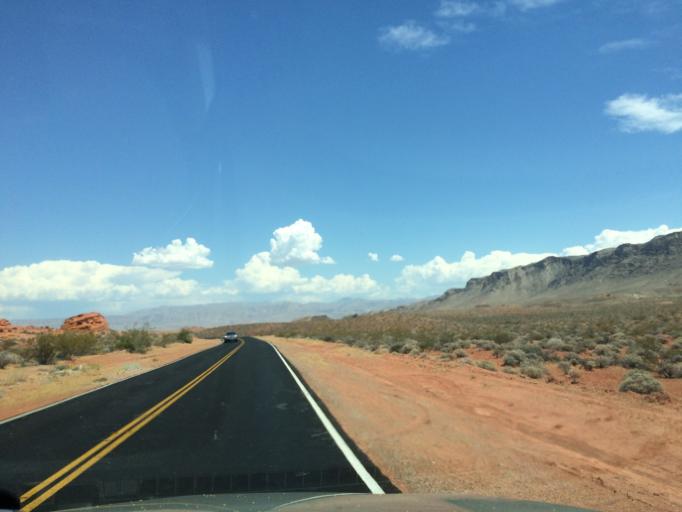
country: US
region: Nevada
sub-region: Clark County
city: Moapa Valley
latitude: 36.4263
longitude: -114.5110
